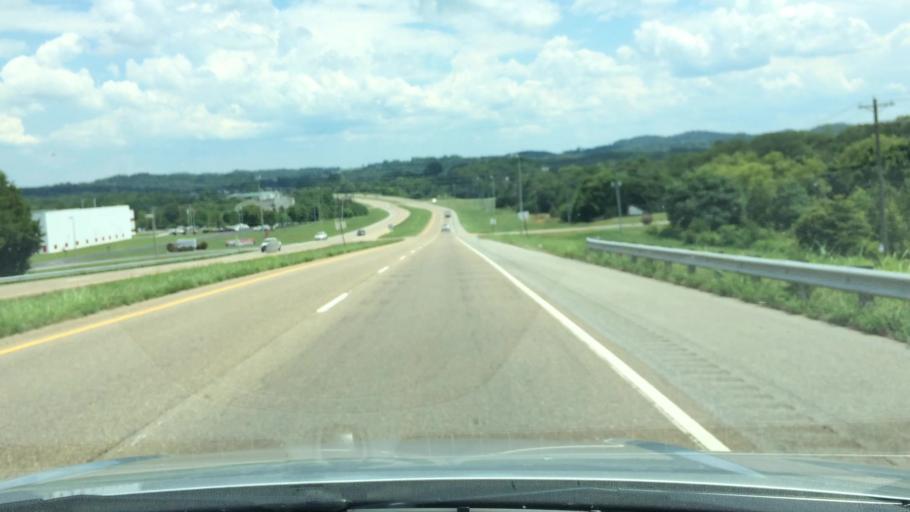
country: US
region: Tennessee
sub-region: Hamblen County
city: Morristown
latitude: 36.1691
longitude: -83.3827
